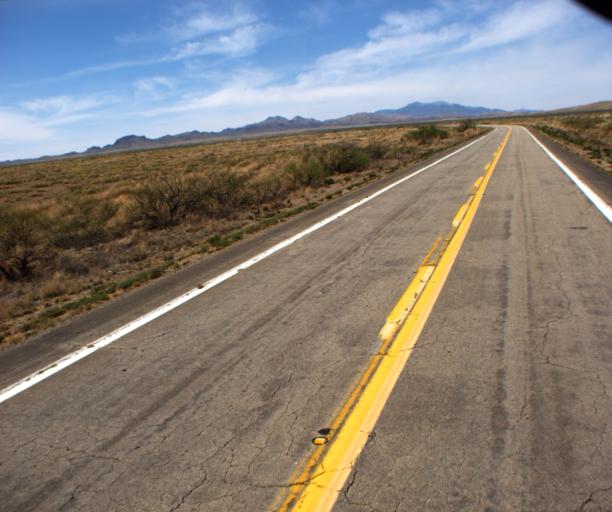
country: US
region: Arizona
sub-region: Cochise County
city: Willcox
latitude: 32.3664
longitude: -109.6231
